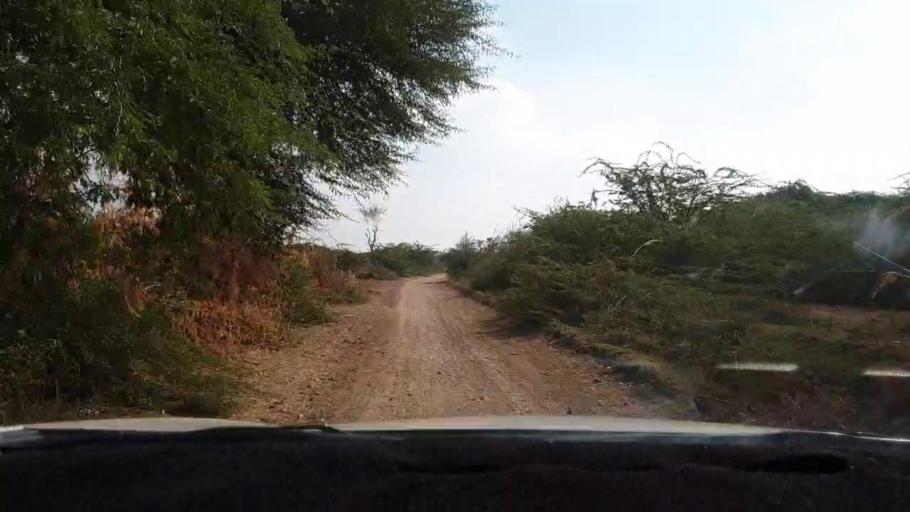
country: PK
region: Sindh
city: Berani
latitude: 25.7621
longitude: 68.9887
